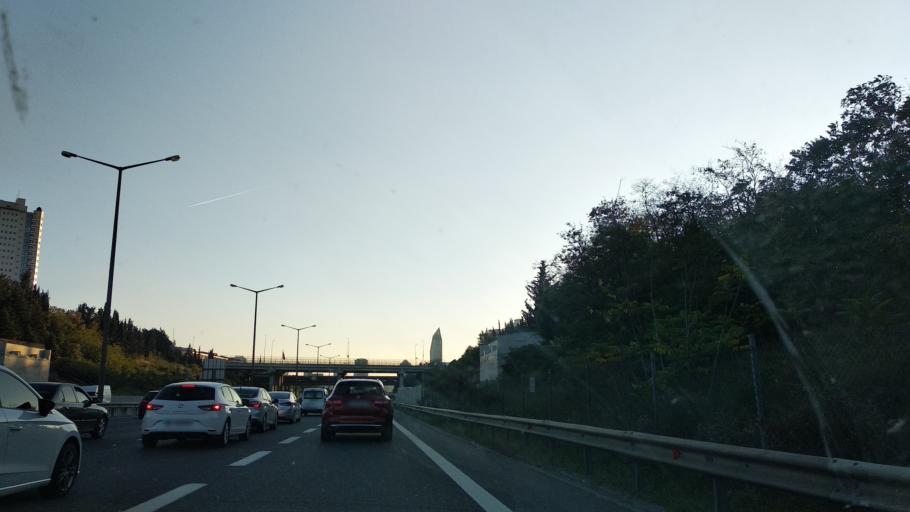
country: TR
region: Istanbul
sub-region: Atasehir
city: Atasehir
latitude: 40.9955
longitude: 29.1155
